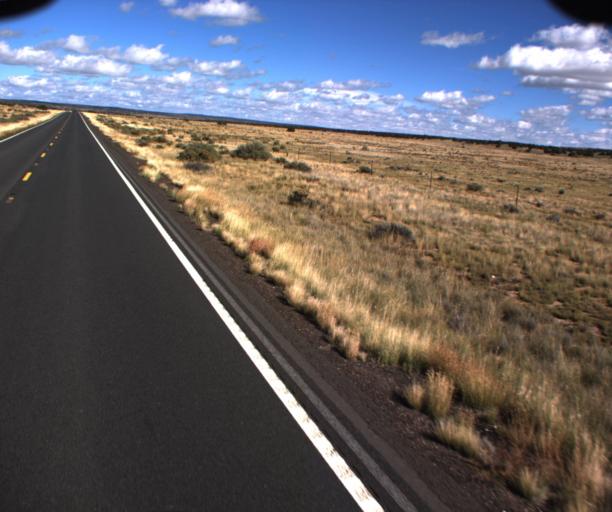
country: US
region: Arizona
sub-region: Apache County
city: Houck
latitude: 34.9852
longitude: -109.2270
